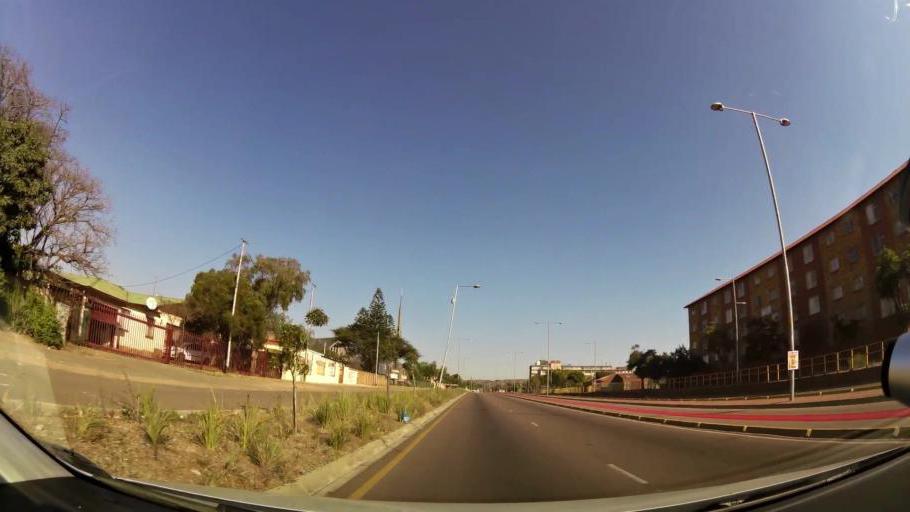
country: ZA
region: Gauteng
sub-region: City of Tshwane Metropolitan Municipality
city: Pretoria
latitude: -25.7107
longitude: 28.1865
